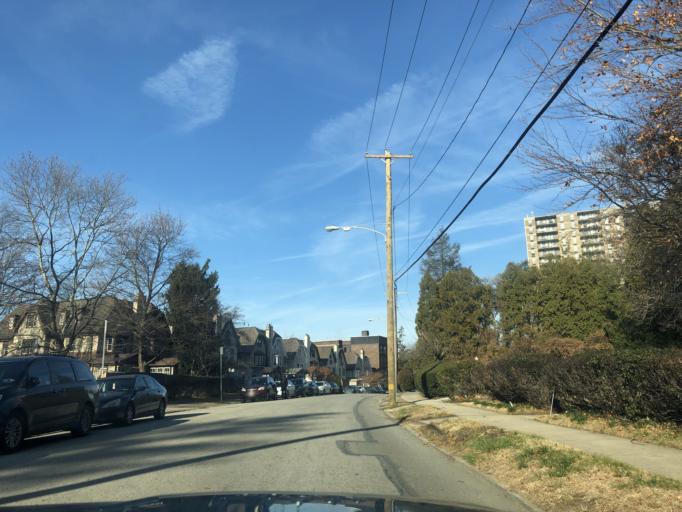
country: US
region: Pennsylvania
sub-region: Montgomery County
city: Bala-Cynwyd
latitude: 39.9886
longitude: -75.2475
